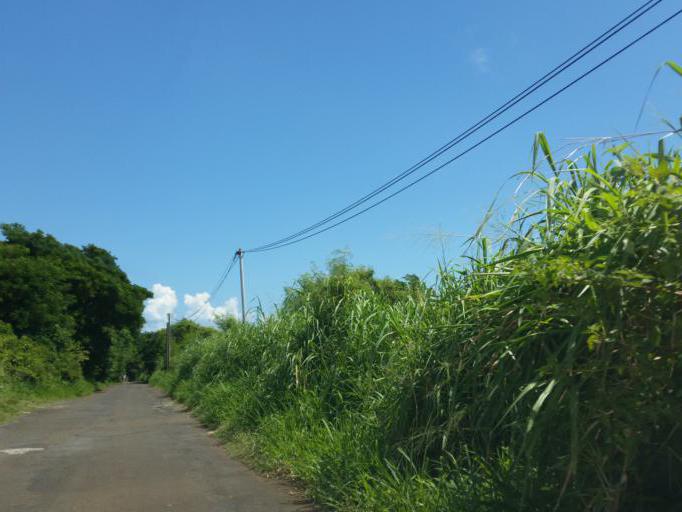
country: RE
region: Reunion
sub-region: Reunion
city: Sainte-Marie
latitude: -20.9096
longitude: 55.5171
